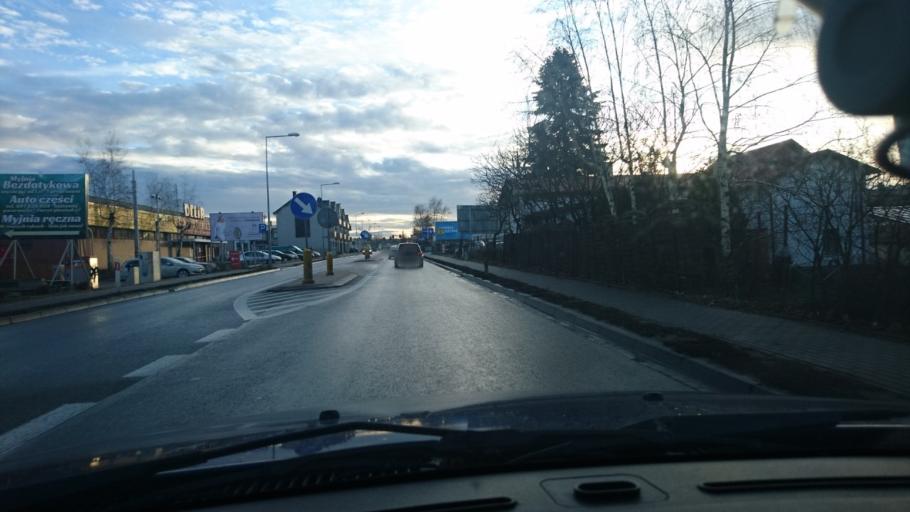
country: PL
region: Greater Poland Voivodeship
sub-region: Powiat kepinski
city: Kepno
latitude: 51.2801
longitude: 17.9918
